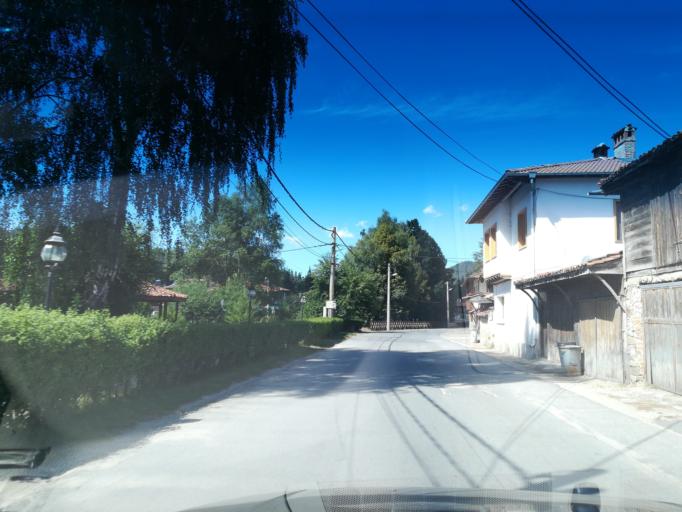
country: BG
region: Sofiya
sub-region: Obshtina Koprivshtitsa
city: Koprivshtitsa
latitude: 42.6378
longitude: 24.3596
